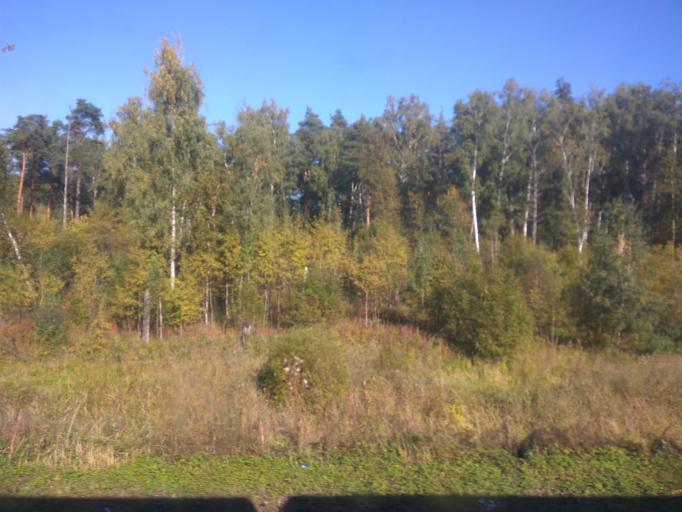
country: RU
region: Moskovskaya
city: Malyshevo
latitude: 55.5176
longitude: 38.3333
